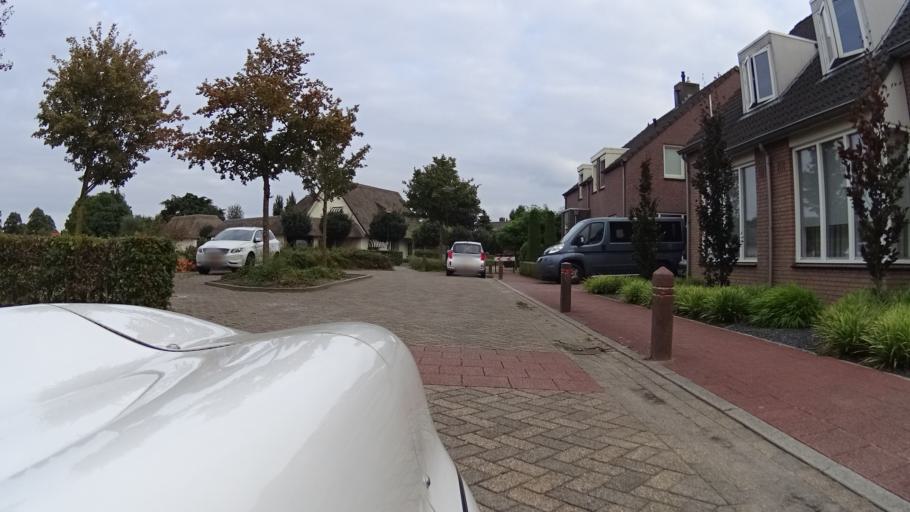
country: NL
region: North Brabant
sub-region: Gemeente Boekel
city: Boekel
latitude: 51.6088
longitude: 5.6756
